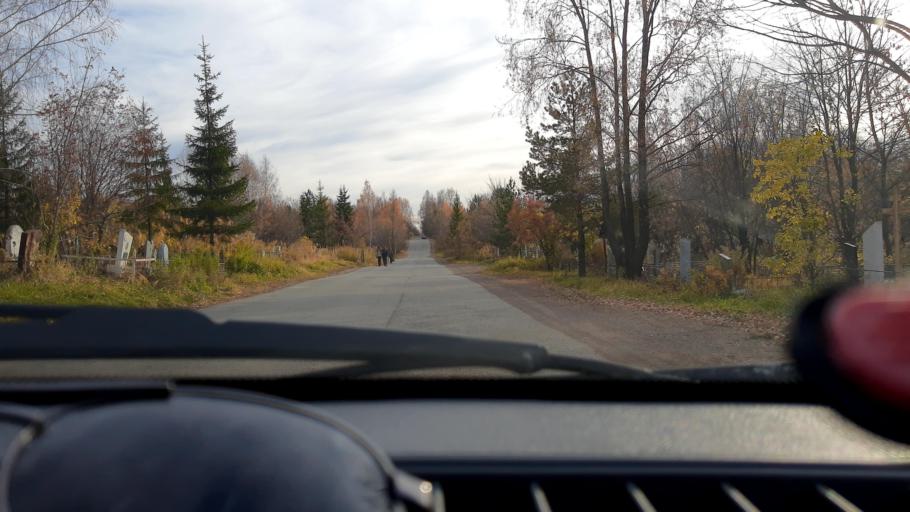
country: RU
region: Bashkortostan
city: Ufa
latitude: 54.8572
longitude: 56.1567
